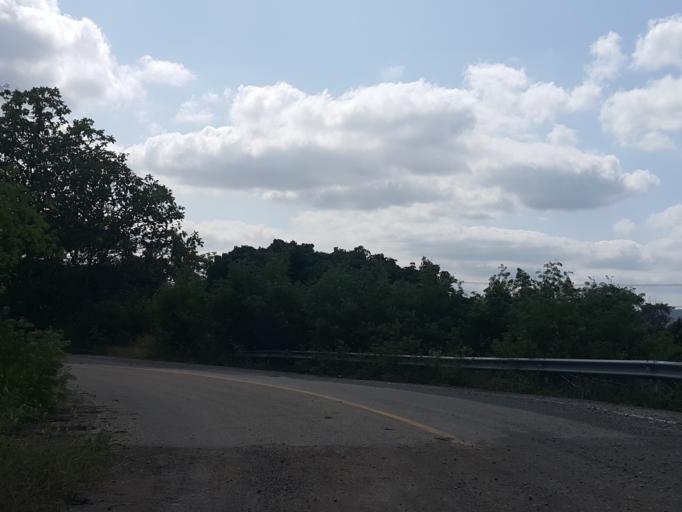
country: TH
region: Lamphun
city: Mae Tha
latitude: 18.5299
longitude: 99.0842
